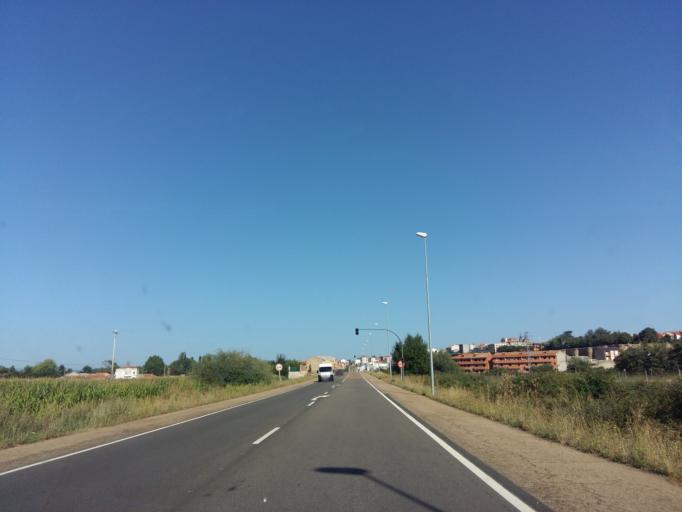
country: ES
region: Castille and Leon
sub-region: Provincia de Leon
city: Astorga
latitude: 42.4480
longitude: -6.0493
